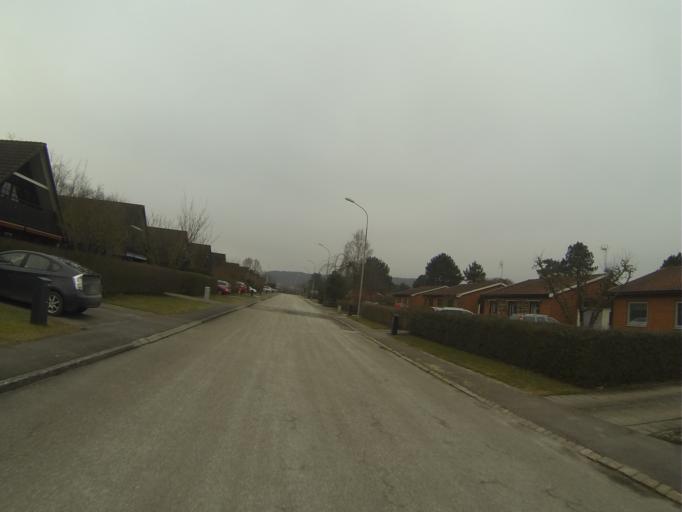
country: SE
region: Skane
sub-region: Lunds Kommun
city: Genarp
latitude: 55.7185
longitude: 13.3606
